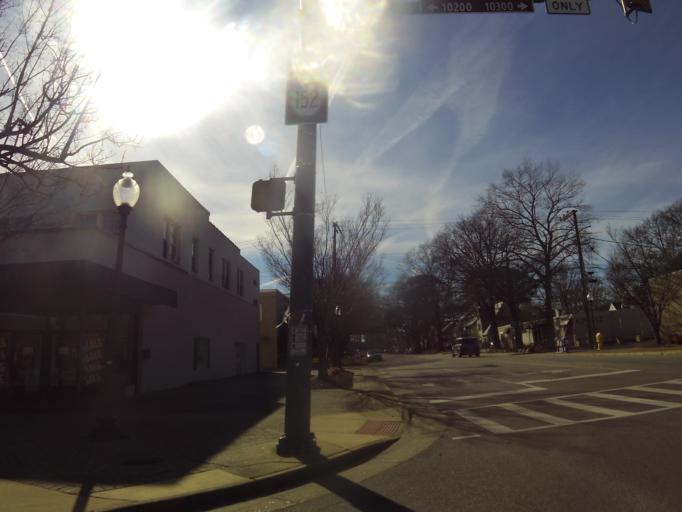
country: US
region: Virginia
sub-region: City of Newport News
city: Newport News
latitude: 37.0323
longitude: -76.4605
